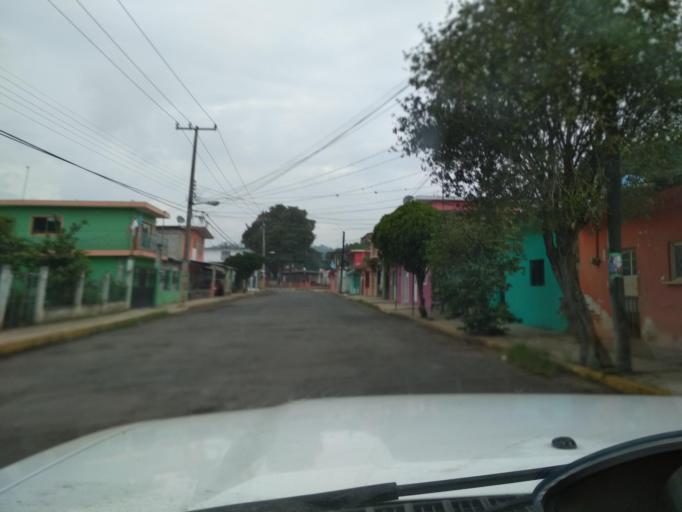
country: MX
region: Veracruz
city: El Castillo
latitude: 19.5644
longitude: -96.8642
